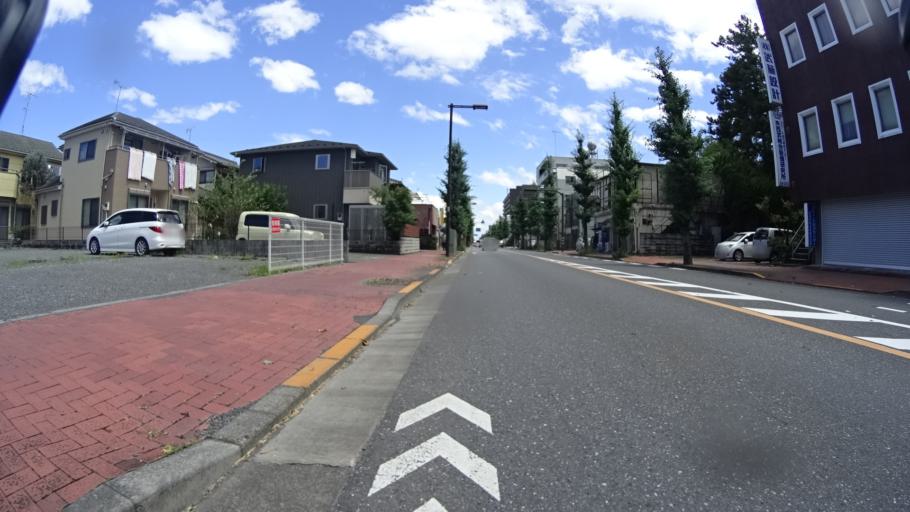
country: JP
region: Tokyo
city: Ome
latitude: 35.7864
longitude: 139.2780
